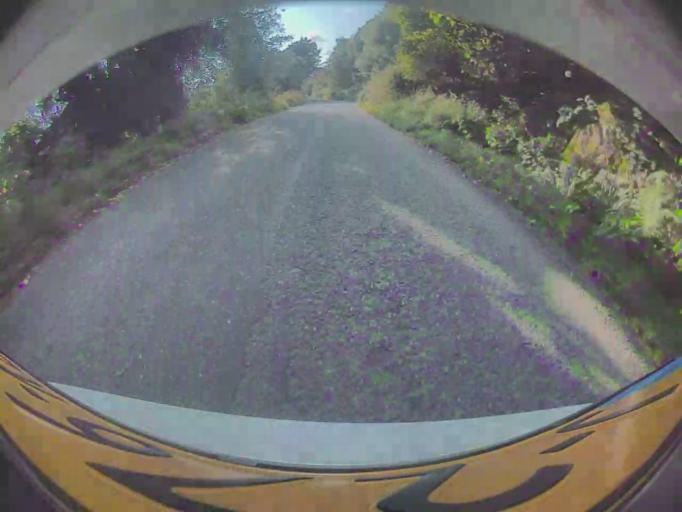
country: IE
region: Leinster
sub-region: Wicklow
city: Enniskerry
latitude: 53.1897
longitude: -6.2398
